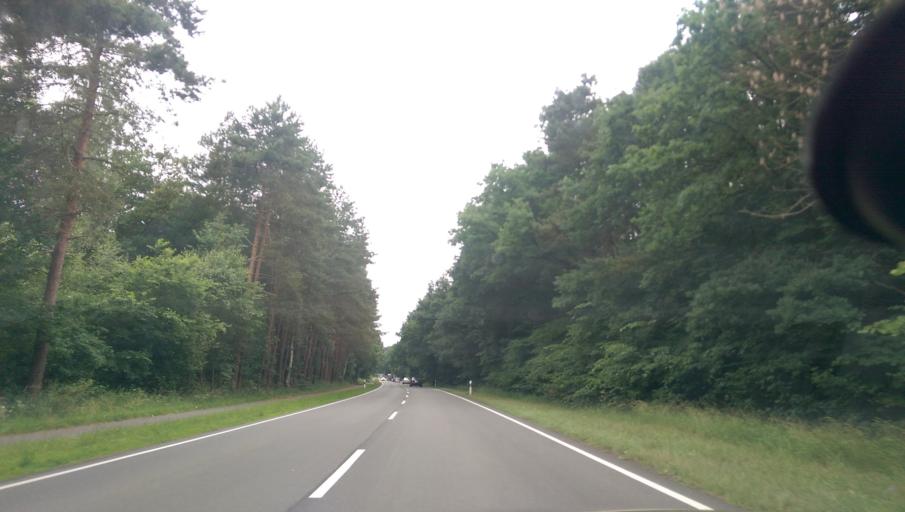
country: DE
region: Lower Saxony
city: Botersen
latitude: 53.1481
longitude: 9.3388
